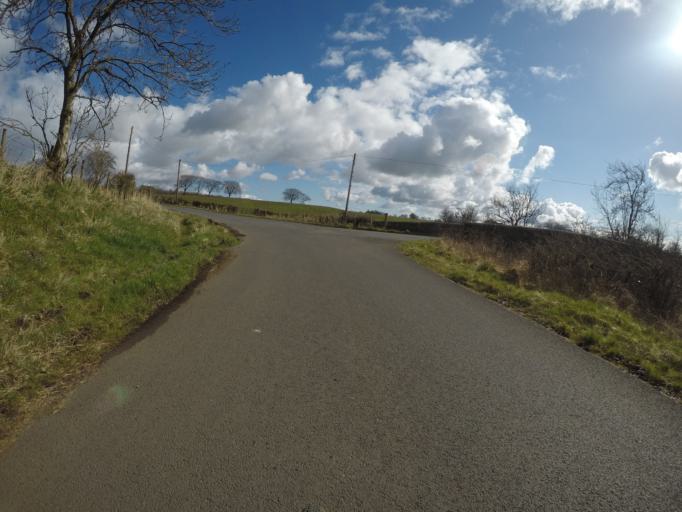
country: GB
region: Scotland
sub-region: North Ayrshire
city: Beith
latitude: 55.7162
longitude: -4.6207
